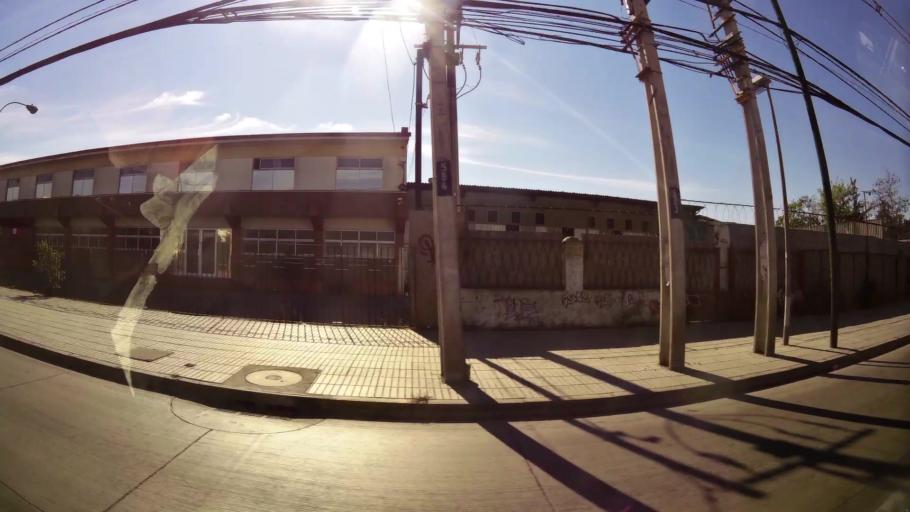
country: CL
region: Santiago Metropolitan
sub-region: Provincia de Santiago
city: Lo Prado
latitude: -33.5052
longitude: -70.7133
